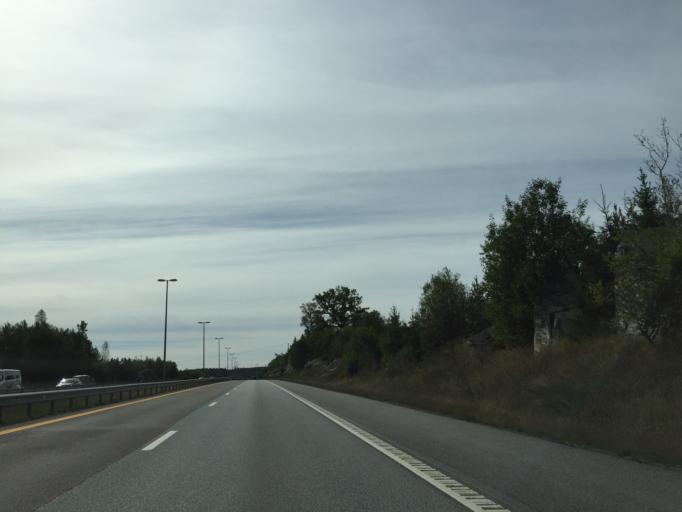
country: NO
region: Akershus
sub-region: Vestby
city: Vestby
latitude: 59.5506
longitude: 10.7226
